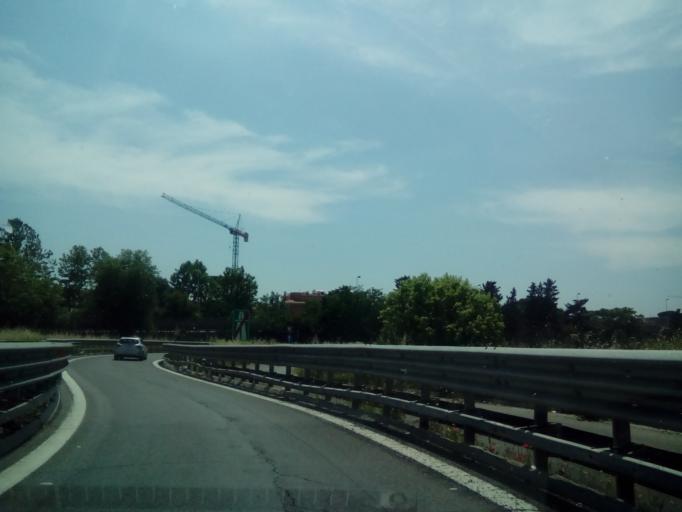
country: IT
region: Latium
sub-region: Citta metropolitana di Roma Capitale
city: Ciampino
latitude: 41.8408
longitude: 12.5900
